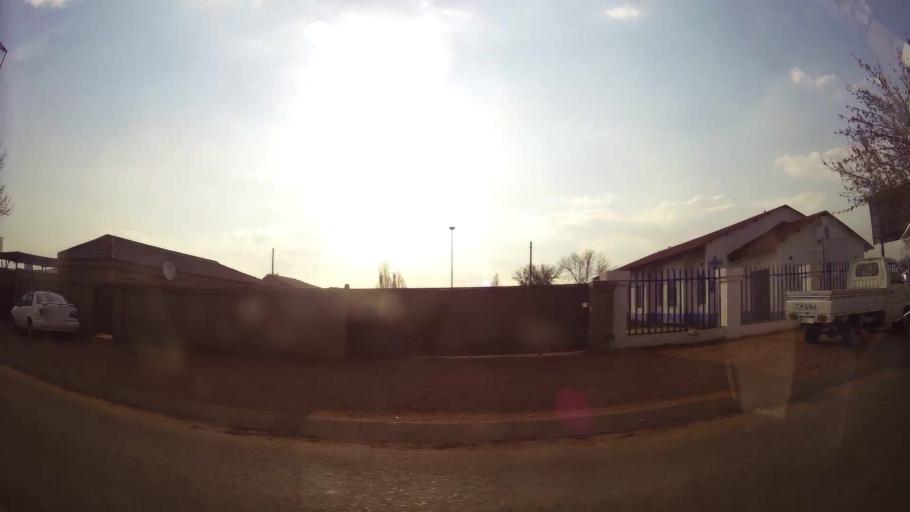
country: ZA
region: Gauteng
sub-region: Ekurhuleni Metropolitan Municipality
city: Germiston
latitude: -26.3571
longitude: 28.1950
